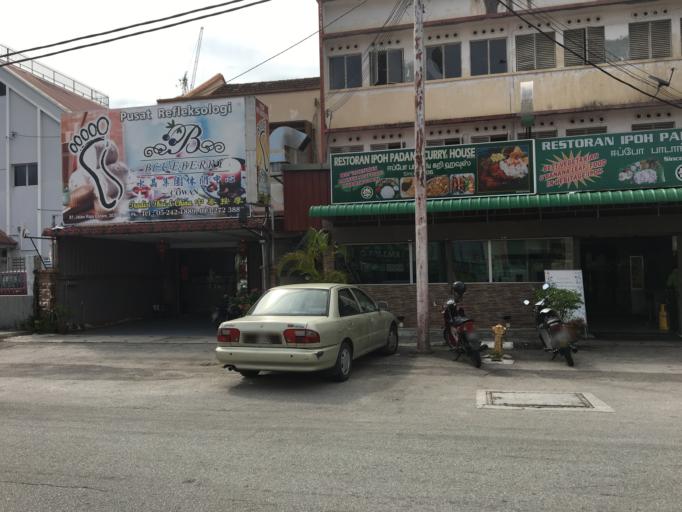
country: MY
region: Perak
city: Ipoh
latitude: 4.5989
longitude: 101.0863
